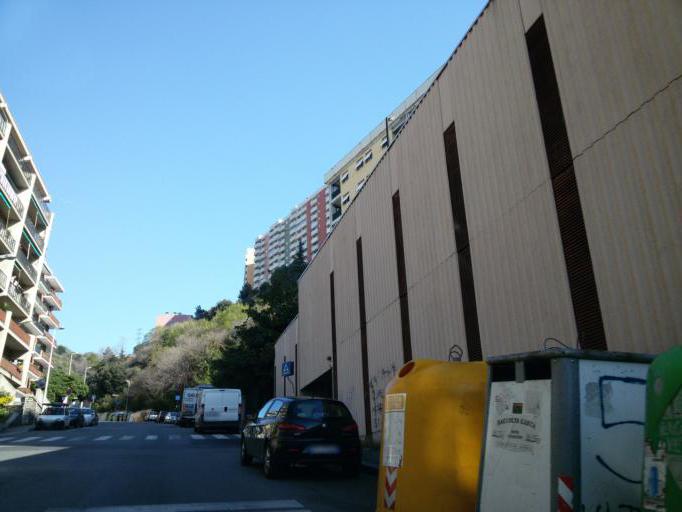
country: IT
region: Liguria
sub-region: Provincia di Genova
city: San Teodoro
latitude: 44.4208
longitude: 8.9095
